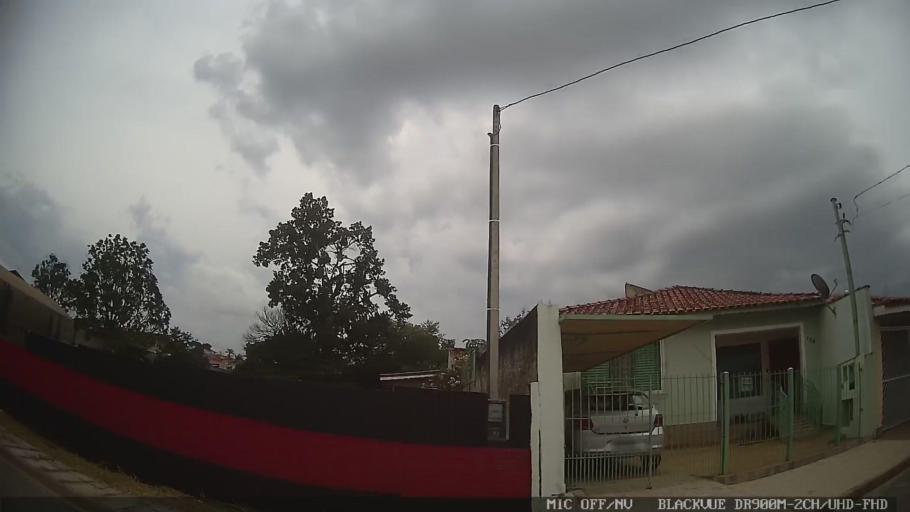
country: BR
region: Sao Paulo
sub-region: Atibaia
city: Atibaia
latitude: -23.1263
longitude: -46.5558
